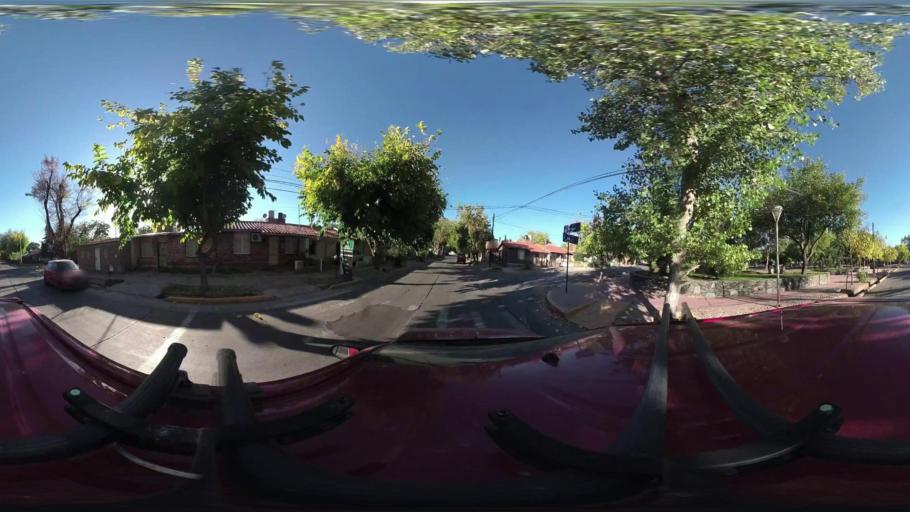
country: AR
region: Mendoza
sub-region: Departamento de Godoy Cruz
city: Godoy Cruz
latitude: -32.9049
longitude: -68.8572
